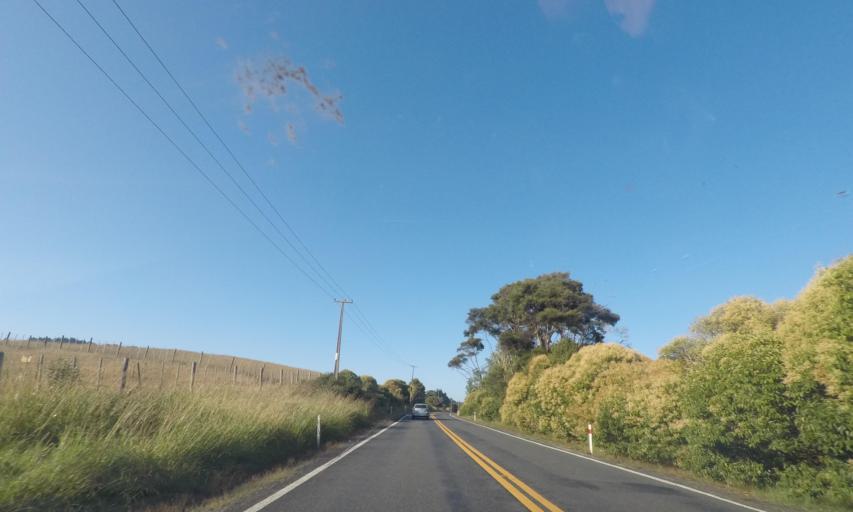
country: NZ
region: Auckland
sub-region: Auckland
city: Muriwai Beach
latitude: -36.7810
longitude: 174.4820
